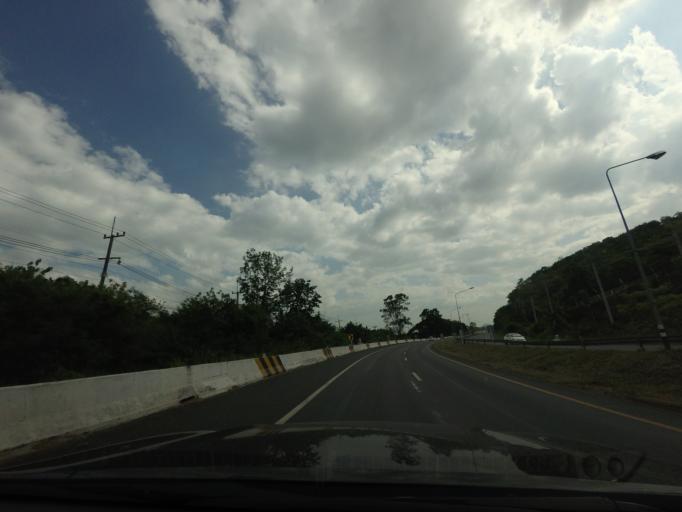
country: TH
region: Lop Buri
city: Chai Badan
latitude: 15.2975
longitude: 101.1295
